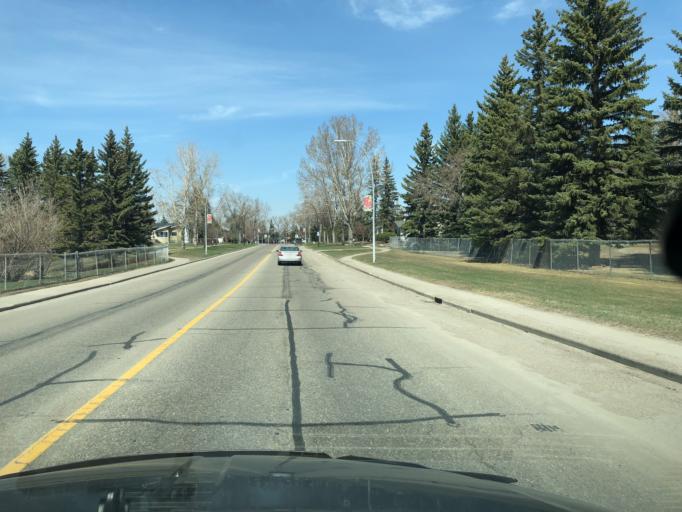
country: CA
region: Alberta
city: Calgary
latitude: 50.9530
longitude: -114.0412
